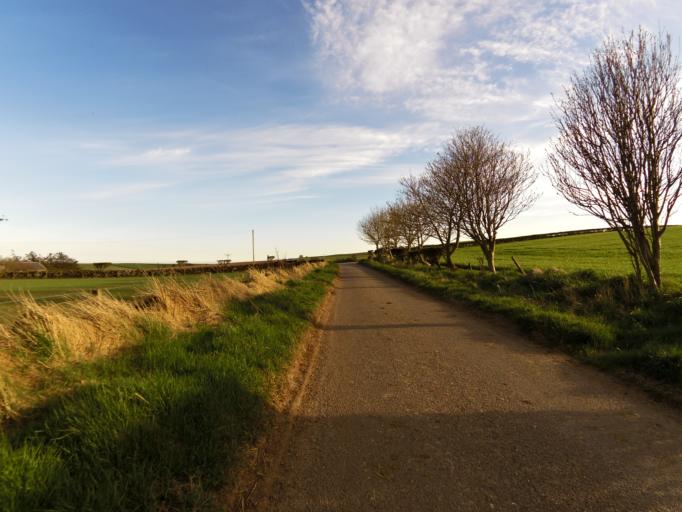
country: GB
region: Scotland
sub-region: Aberdeenshire
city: Inverbervie
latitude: 56.8867
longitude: -2.2375
